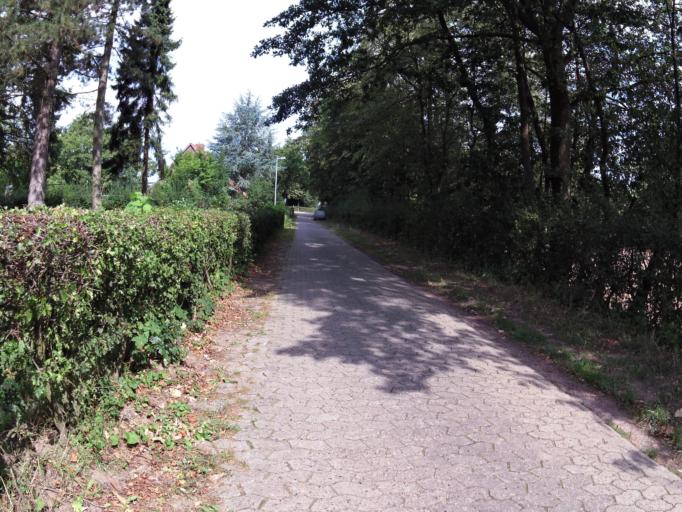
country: DE
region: Lower Saxony
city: Landesbergen
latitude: 52.5751
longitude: 9.1137
